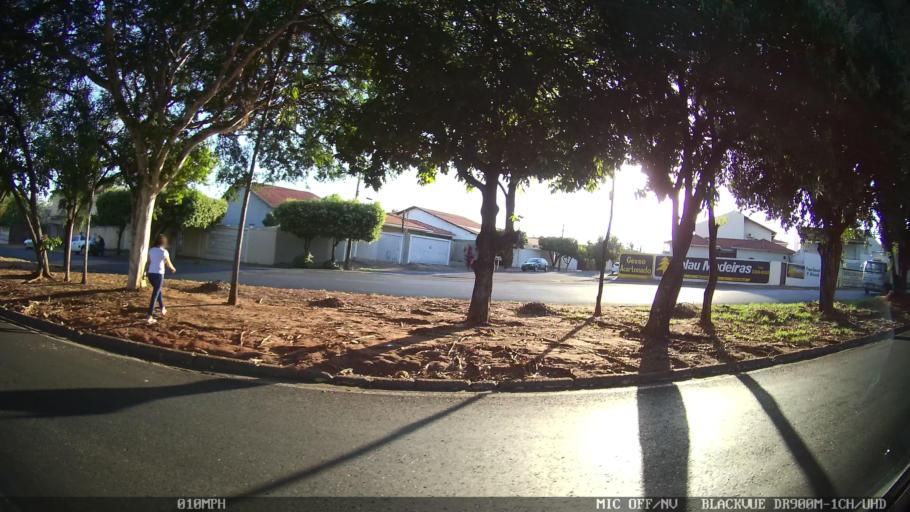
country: BR
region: Sao Paulo
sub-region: Sao Jose Do Rio Preto
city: Sao Jose do Rio Preto
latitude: -20.7943
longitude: -49.3577
